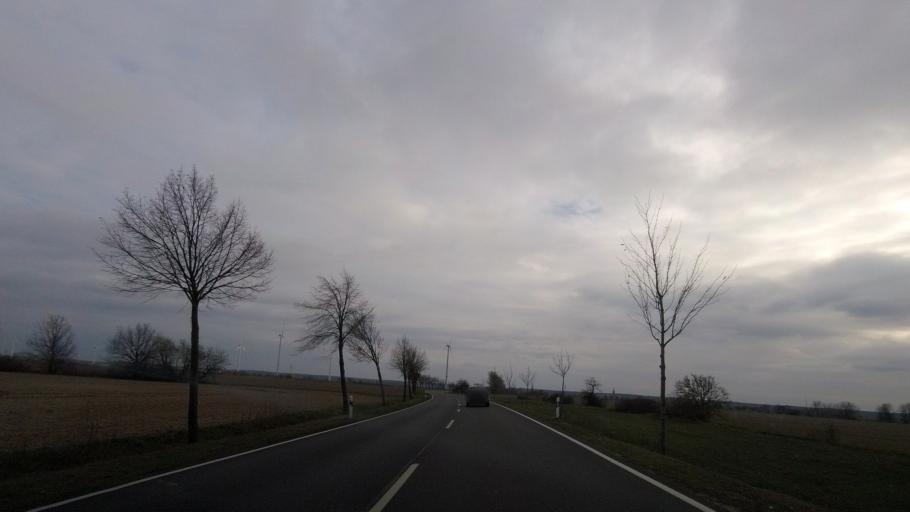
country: DE
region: Saxony-Anhalt
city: Kemberg
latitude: 51.7971
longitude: 12.6515
